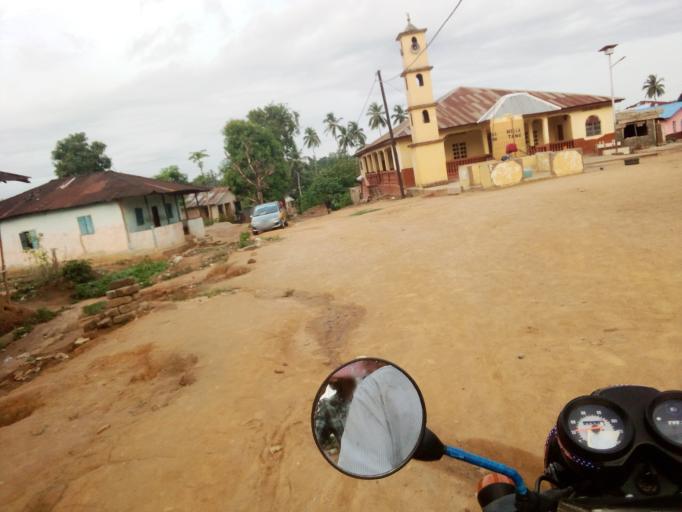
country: SL
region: Western Area
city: Waterloo
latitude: 8.3338
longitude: -13.0690
